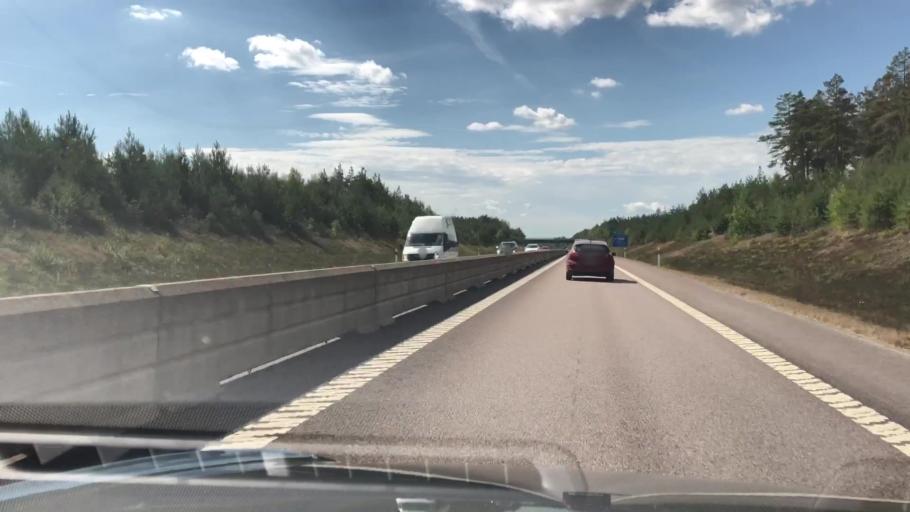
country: SE
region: Kalmar
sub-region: Kalmar Kommun
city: Ljungbyholm
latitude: 56.5975
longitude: 16.1271
